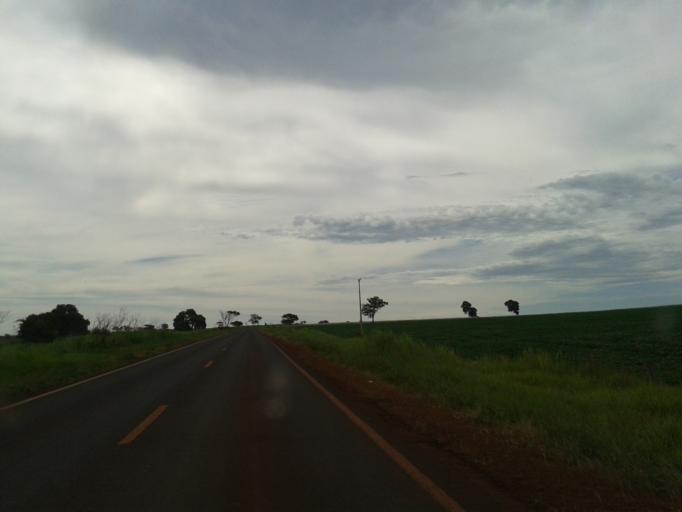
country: BR
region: Minas Gerais
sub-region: Capinopolis
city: Capinopolis
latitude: -18.6907
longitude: -49.3778
